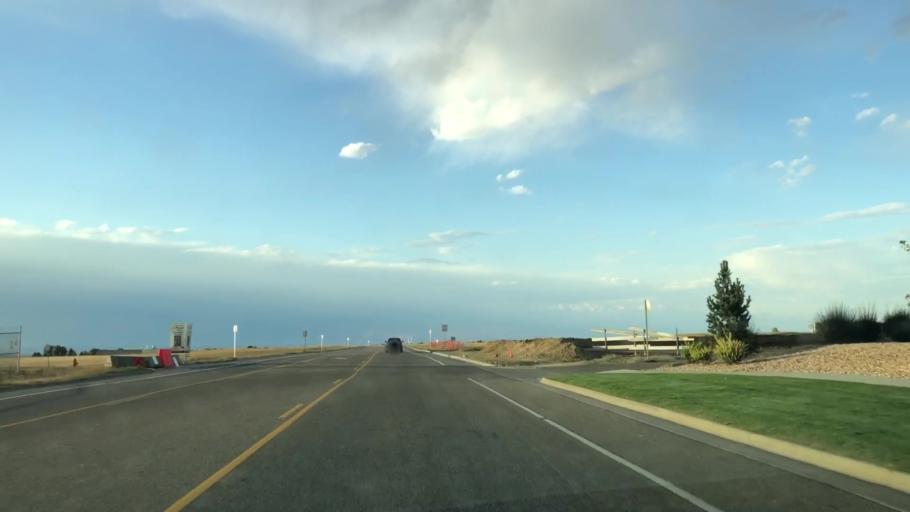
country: US
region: Colorado
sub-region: Larimer County
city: Loveland
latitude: 40.4383
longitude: -104.9958
